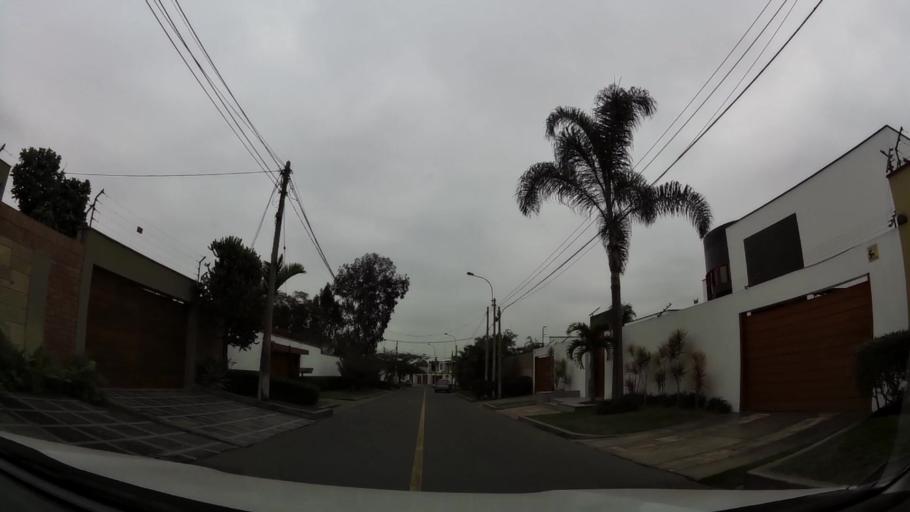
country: PE
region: Lima
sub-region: Lima
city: La Molina
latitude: -12.0860
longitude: -76.9232
